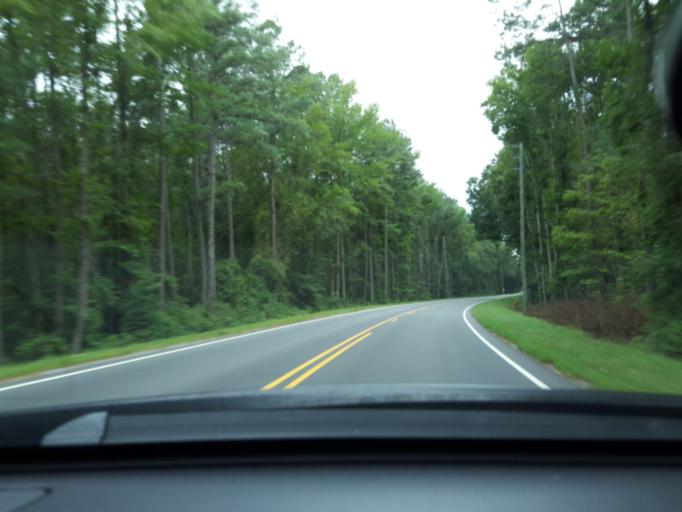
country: US
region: North Carolina
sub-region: Sampson County
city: Roseboro
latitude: 34.7650
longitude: -78.4046
